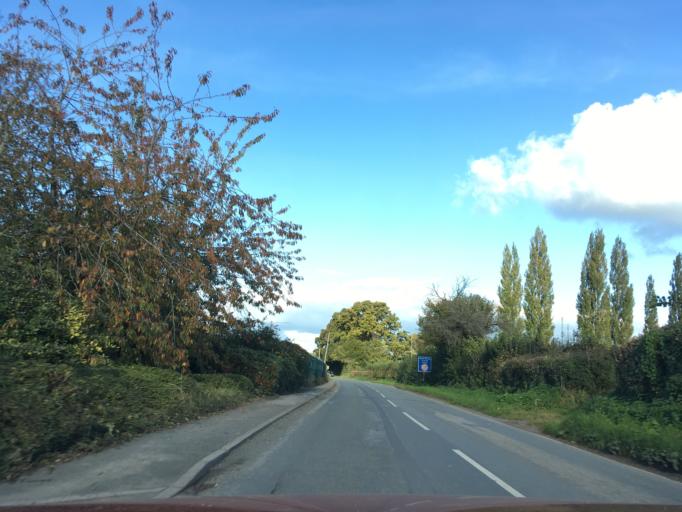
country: GB
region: Wales
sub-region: Sir Powys
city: Hay
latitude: 52.0798
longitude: -3.1223
